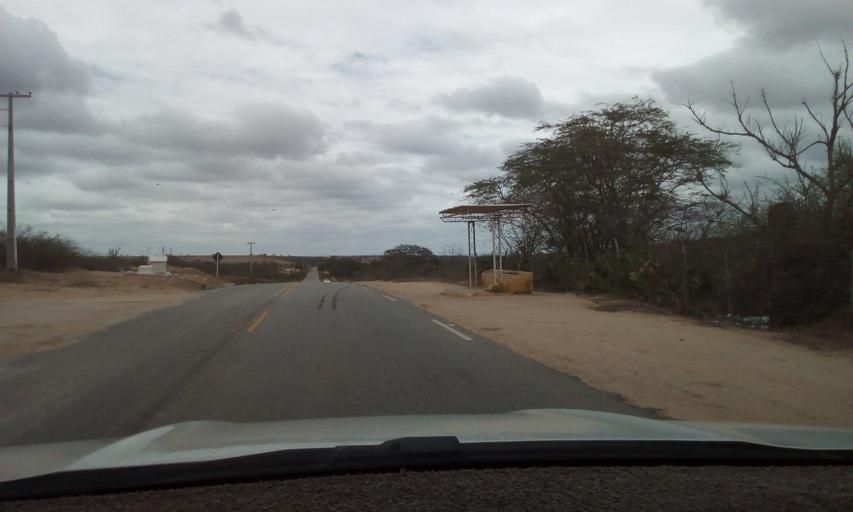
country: BR
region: Paraiba
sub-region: Picui
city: Picui
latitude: -6.5619
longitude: -36.2836
